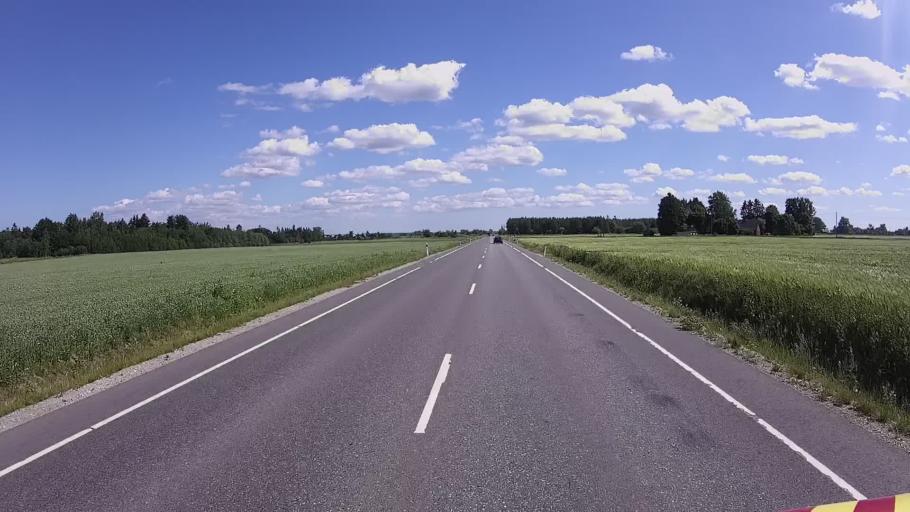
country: EE
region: Ida-Virumaa
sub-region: Johvi vald
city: Johvi
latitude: 59.3376
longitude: 27.3672
